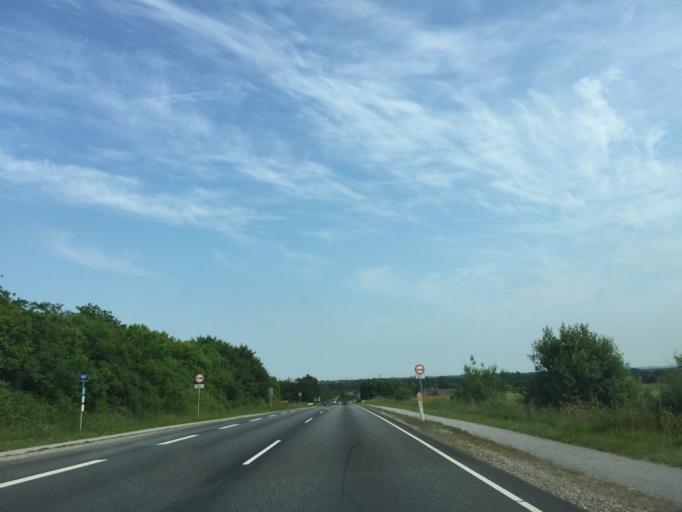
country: DK
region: Central Jutland
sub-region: Arhus Kommune
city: Sabro
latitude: 56.2058
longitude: 10.0429
